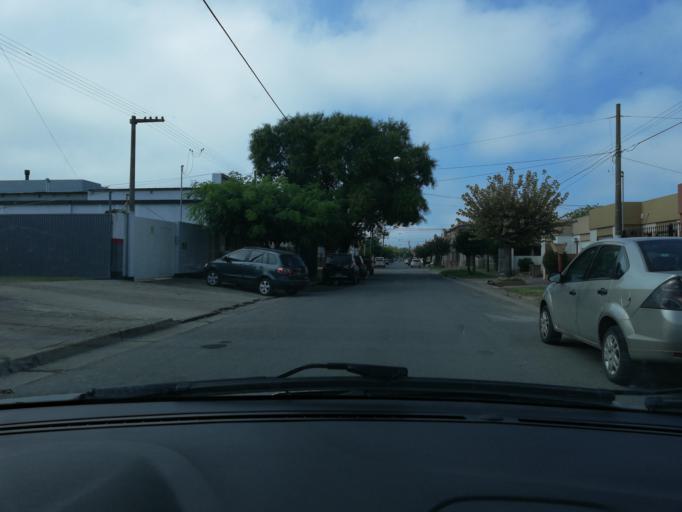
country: AR
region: Buenos Aires
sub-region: Partido de Balcarce
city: Balcarce
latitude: -37.8384
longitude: -58.2618
